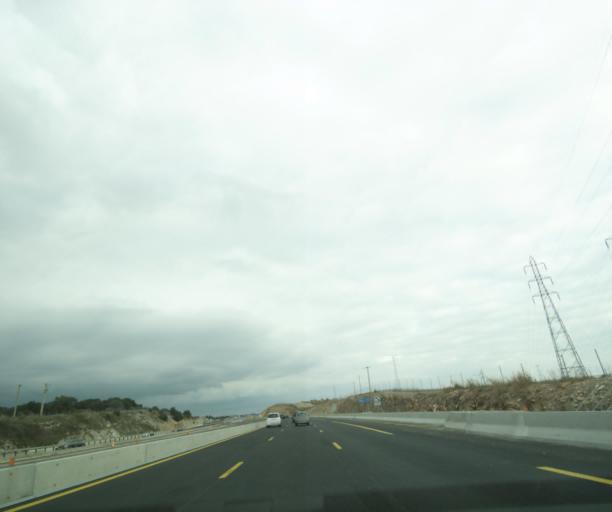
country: FR
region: Languedoc-Roussillon
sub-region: Departement de l'Herault
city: Saint-Jean-de-Vedas
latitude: 43.5540
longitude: 3.8214
